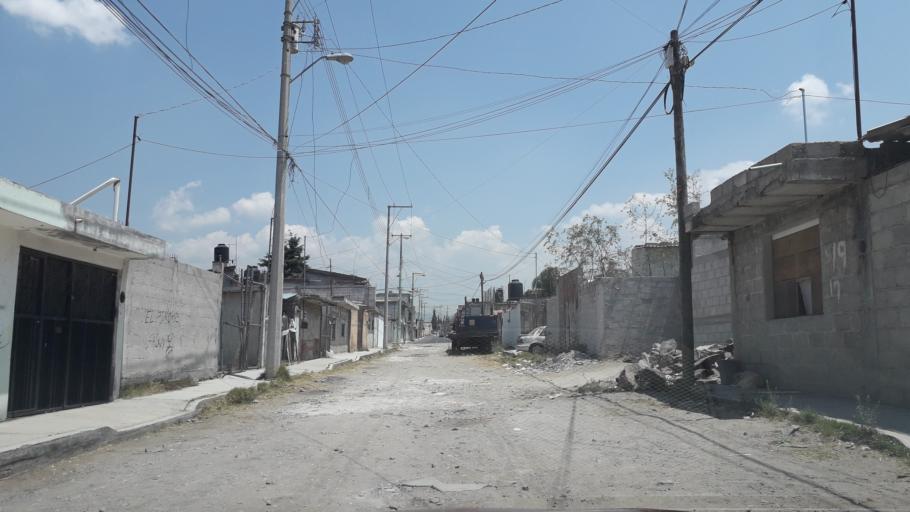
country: MX
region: Puebla
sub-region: Amozoc
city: Casa Blanca
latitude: 19.0693
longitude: -98.1222
